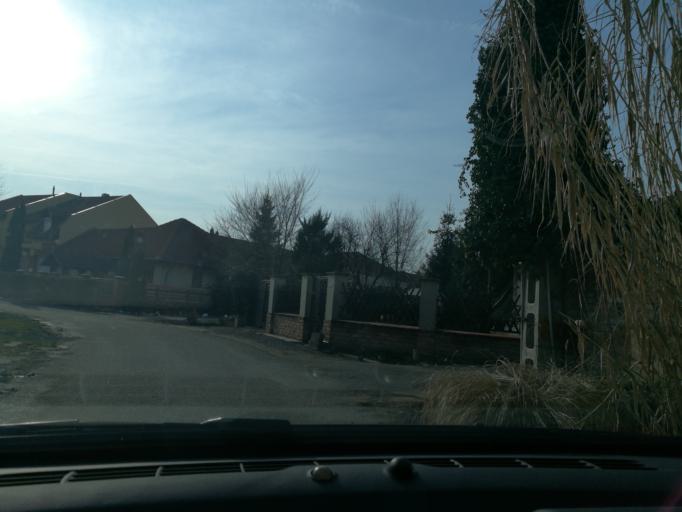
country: HU
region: Szabolcs-Szatmar-Bereg
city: Nyiregyhaza
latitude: 47.9659
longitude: 21.7393
